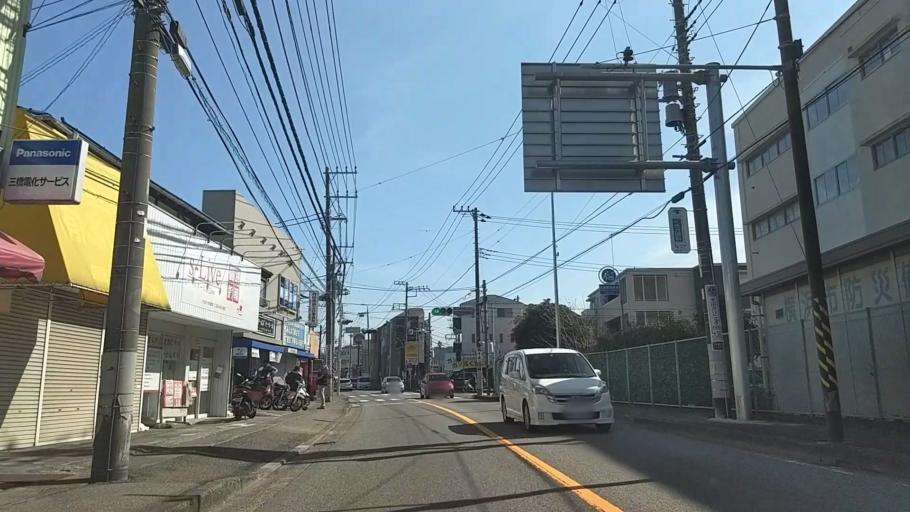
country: JP
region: Kanagawa
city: Kamakura
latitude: 35.3633
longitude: 139.5617
